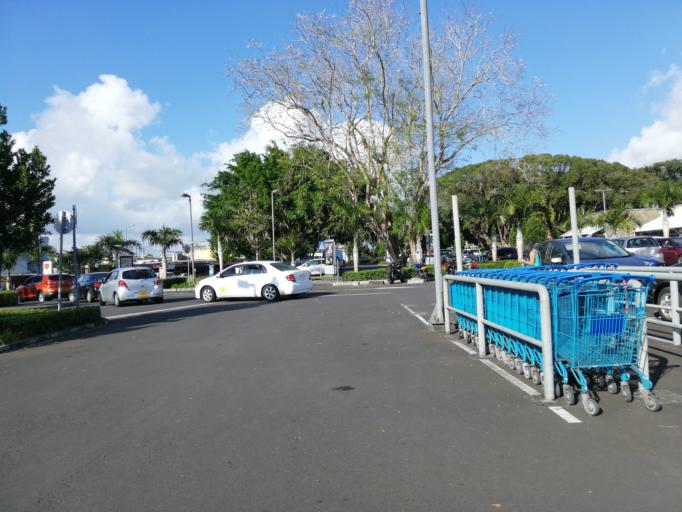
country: MU
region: Moka
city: Verdun
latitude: -20.2256
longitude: 57.5378
